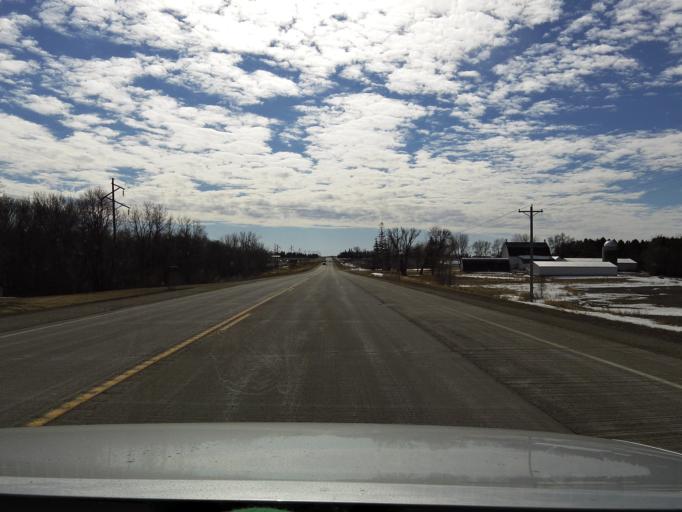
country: US
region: Minnesota
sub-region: Le Sueur County
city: New Prague
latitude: 44.5274
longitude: -93.5856
